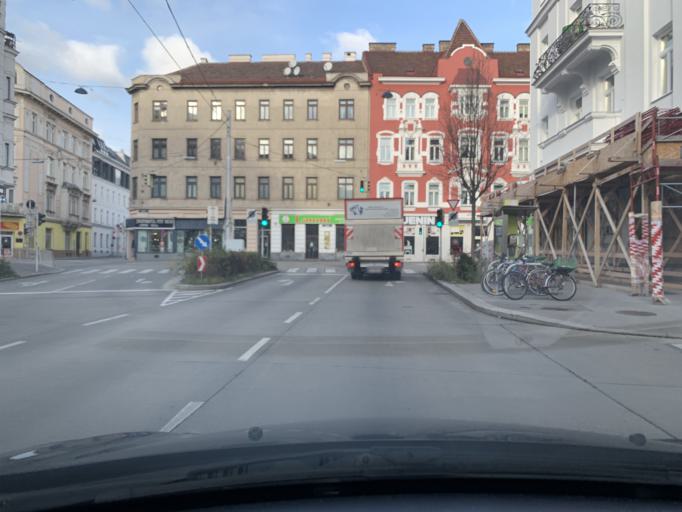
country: AT
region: Vienna
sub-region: Wien Stadt
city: Vienna
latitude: 48.1876
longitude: 16.3340
